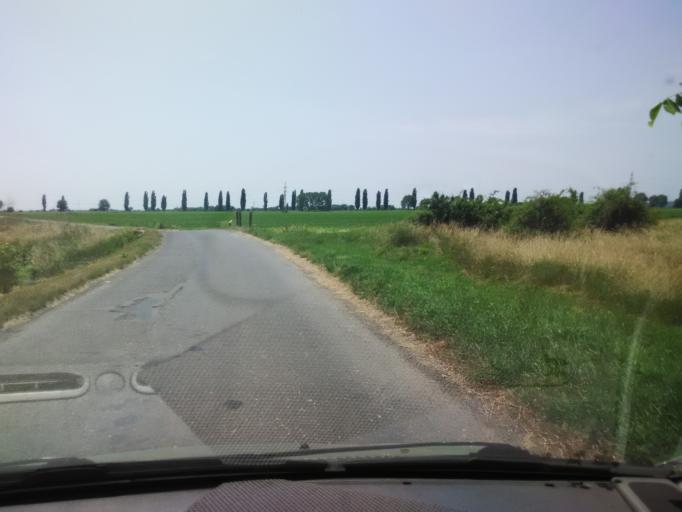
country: SK
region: Nitriansky
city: Tlmace
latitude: 48.2670
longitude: 18.5779
